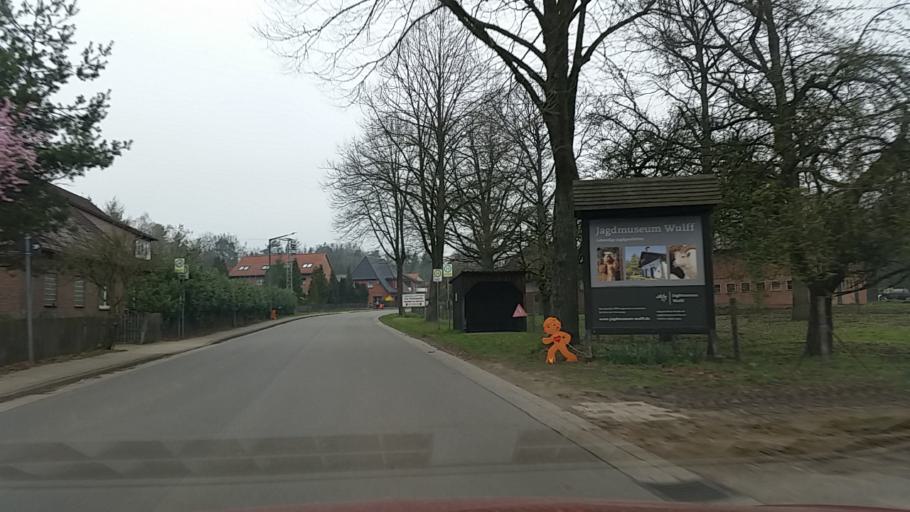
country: DE
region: Lower Saxony
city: Hankensbuttel
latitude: 52.6787
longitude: 10.5751
